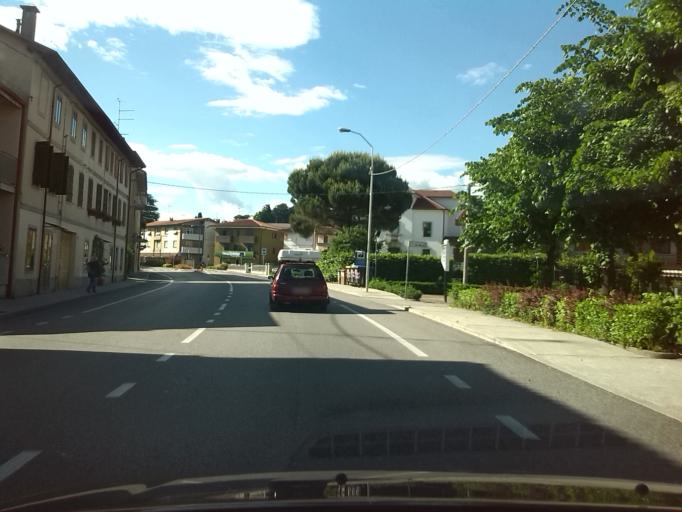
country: IT
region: Friuli Venezia Giulia
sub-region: Provincia di Udine
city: Tricesimo
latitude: 46.1571
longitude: 13.2182
